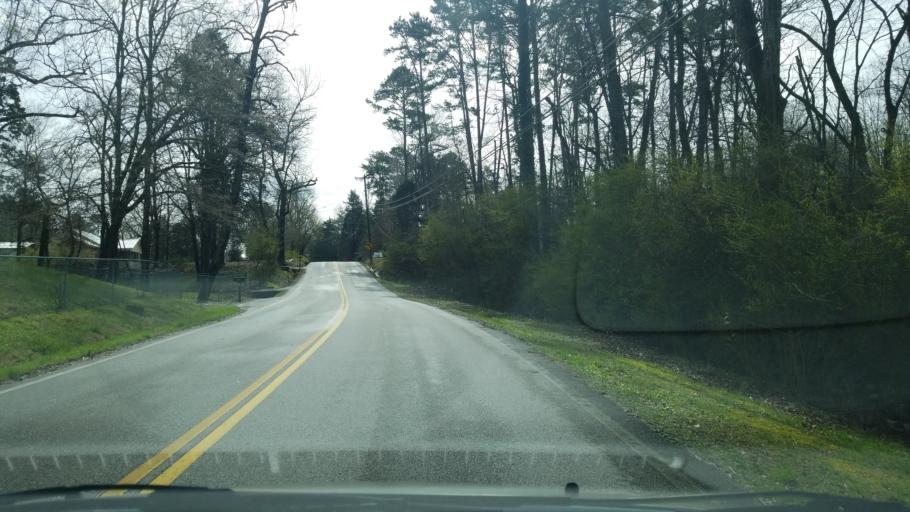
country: US
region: Tennessee
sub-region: Hamilton County
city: Harrison
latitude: 35.1405
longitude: -85.0901
